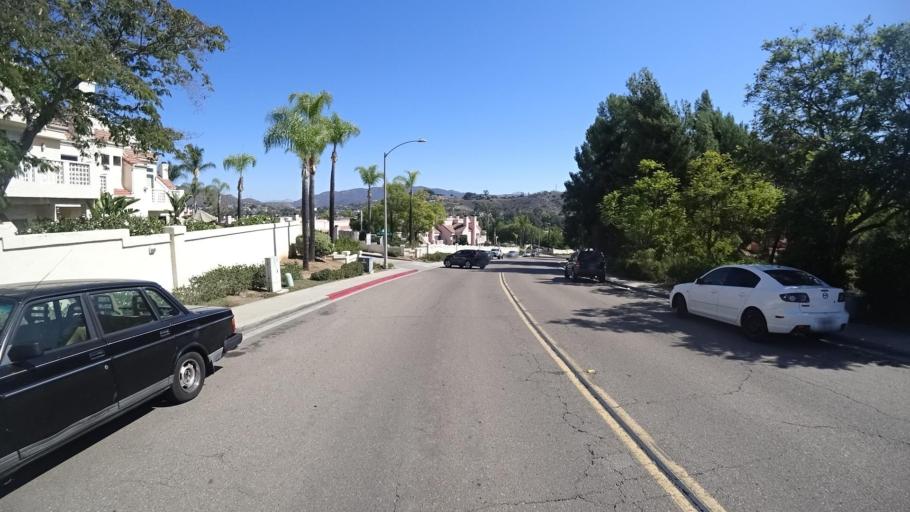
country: US
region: California
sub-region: San Diego County
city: Rancho San Diego
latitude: 32.7545
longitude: -116.9307
